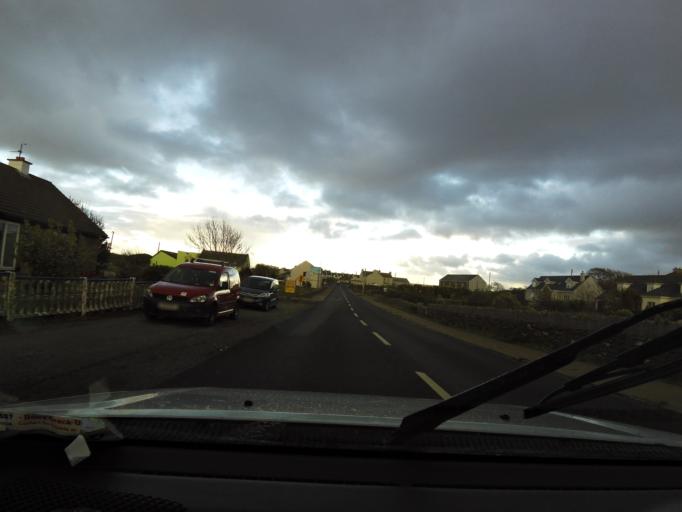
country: IE
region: Munster
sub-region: An Clar
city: Kilrush
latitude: 52.9388
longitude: -9.3964
